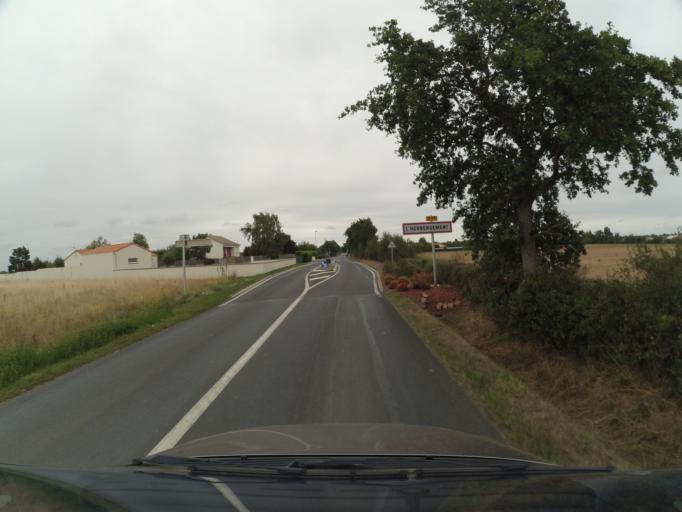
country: FR
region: Pays de la Loire
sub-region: Departement de la Vendee
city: Saint-Andre-Treize-Voies
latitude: 46.9162
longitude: -1.3858
